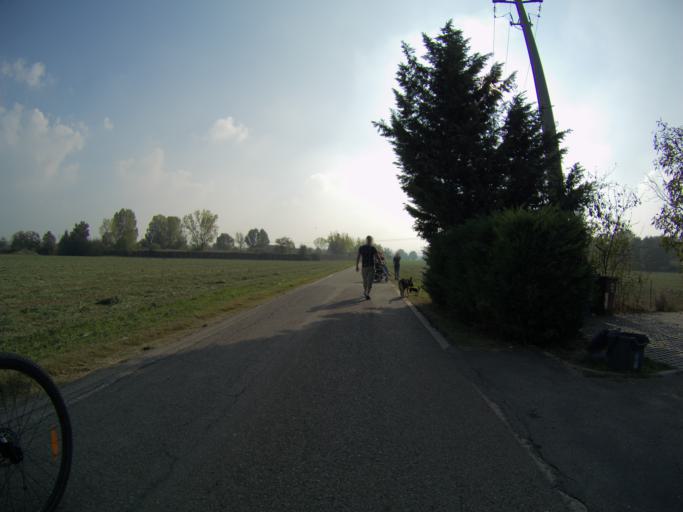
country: IT
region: Emilia-Romagna
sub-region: Provincia di Reggio Emilia
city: Forche
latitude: 44.6532
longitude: 10.5699
